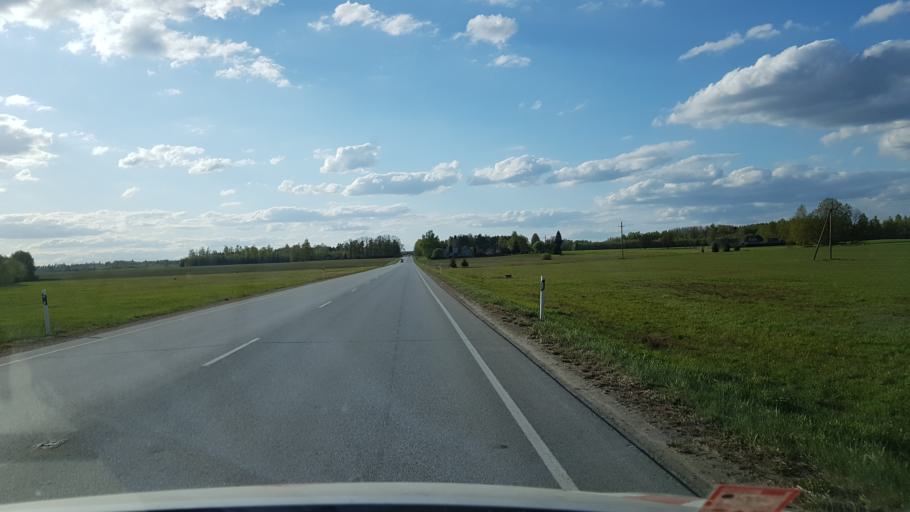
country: EE
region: Vorumaa
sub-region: Voru linn
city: Voru
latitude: 57.9100
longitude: 26.8253
